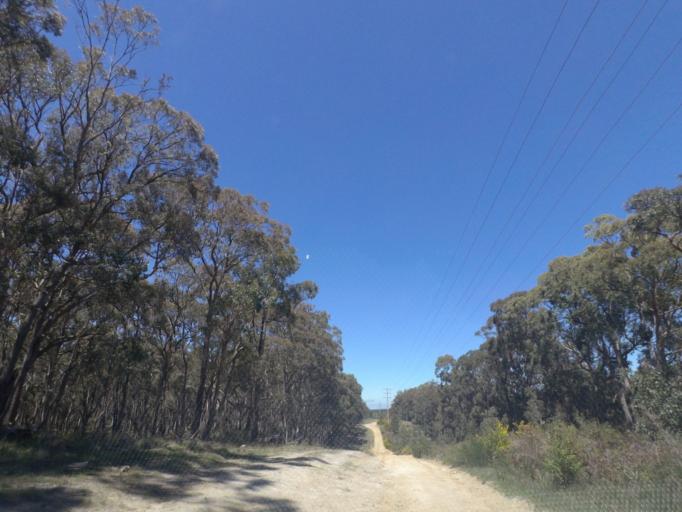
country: AU
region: Victoria
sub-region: Hume
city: Sunbury
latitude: -37.3844
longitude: 144.5516
